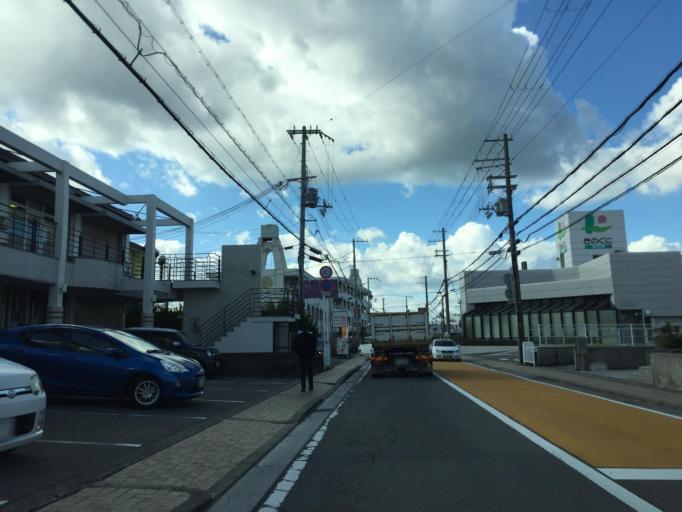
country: JP
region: Wakayama
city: Kainan
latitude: 34.1717
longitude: 135.1941
